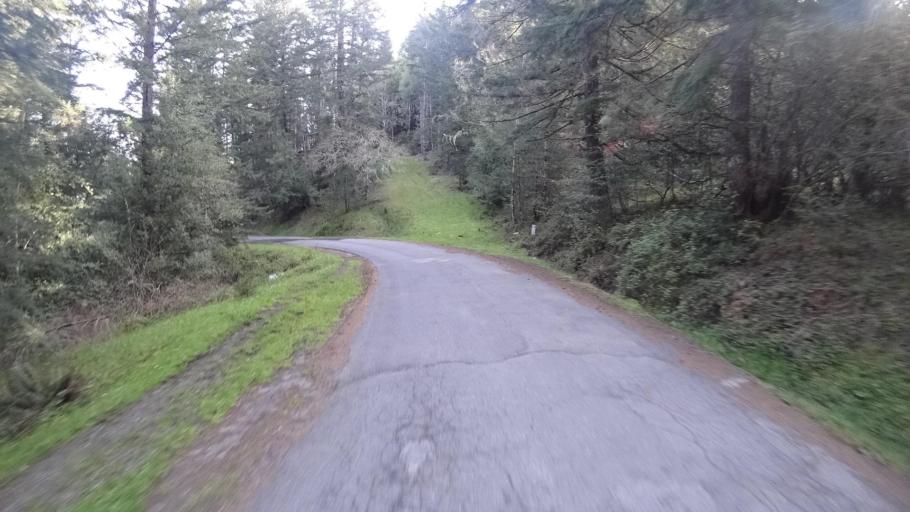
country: US
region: California
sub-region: Humboldt County
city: Hydesville
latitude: 40.6782
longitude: -123.9382
